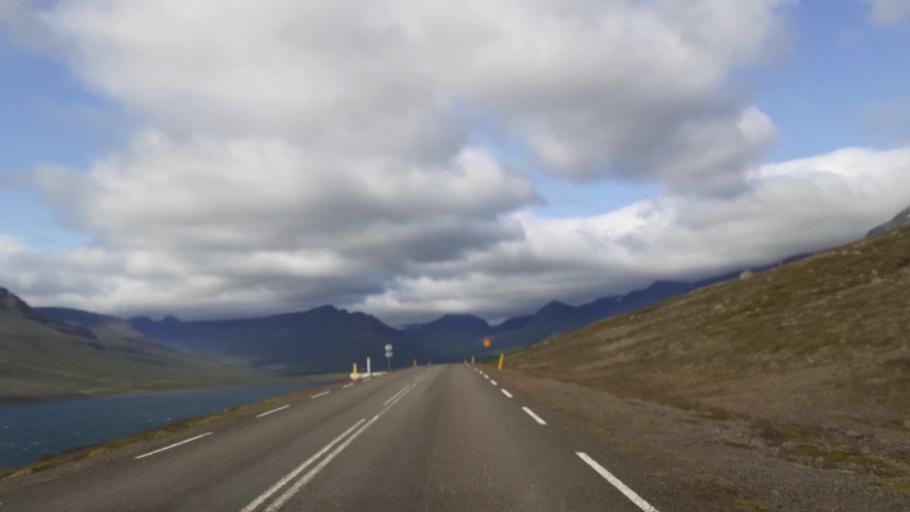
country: IS
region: East
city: Eskifjoerdur
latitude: 64.9229
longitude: -13.9759
